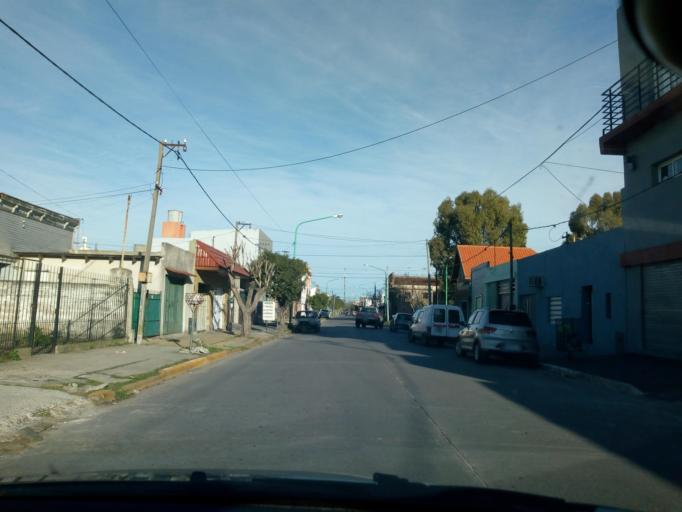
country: AR
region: Buenos Aires
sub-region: Partido de Ensenada
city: Ensenada
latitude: -34.8584
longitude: -57.9043
